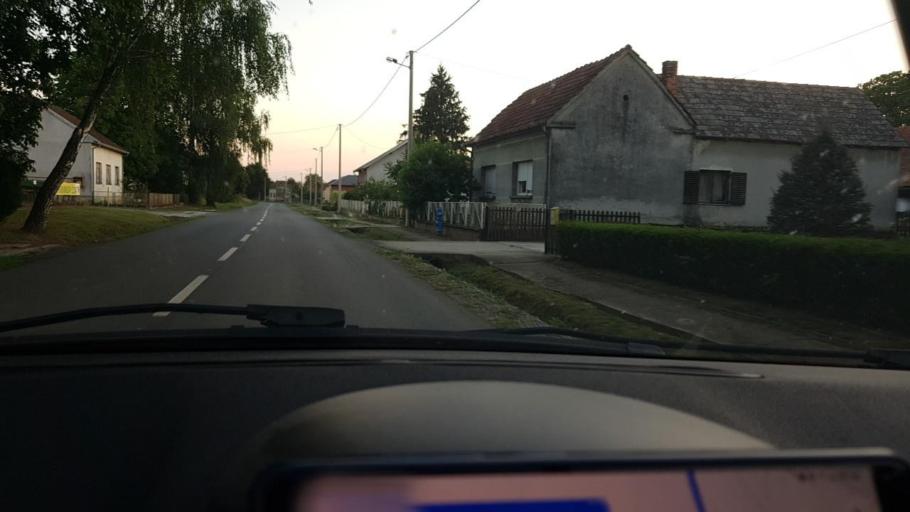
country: HR
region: Bjelovarsko-Bilogorska
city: Zdralovi
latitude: 45.8479
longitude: 16.9752
